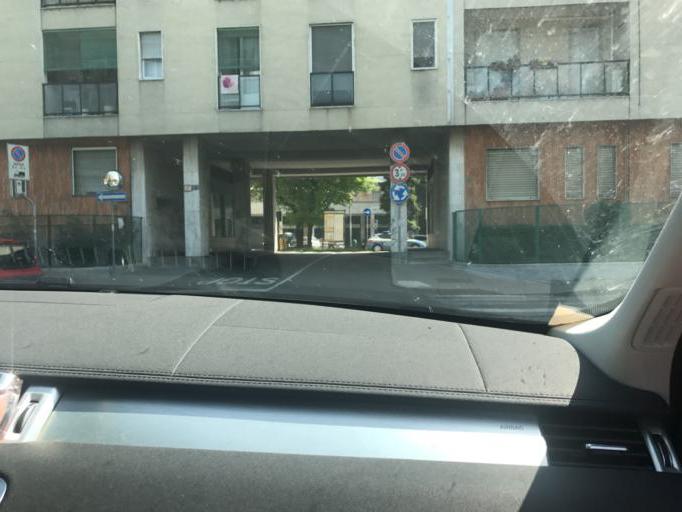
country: IT
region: Lombardy
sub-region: Citta metropolitana di Milano
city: Romano Banco
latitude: 45.4435
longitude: 9.1133
